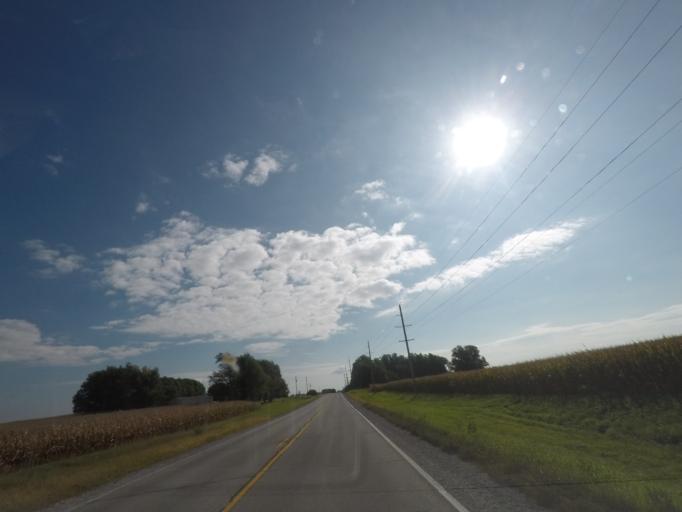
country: US
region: Iowa
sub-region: Story County
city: Nevada
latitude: 42.0227
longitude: -93.4210
